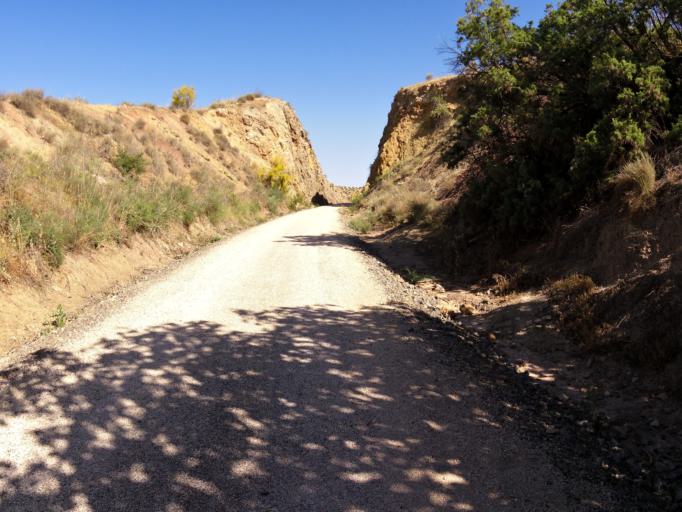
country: ES
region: Andalusia
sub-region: Provincia de Jaen
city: Alcaudete
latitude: 37.6013
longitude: -4.1582
